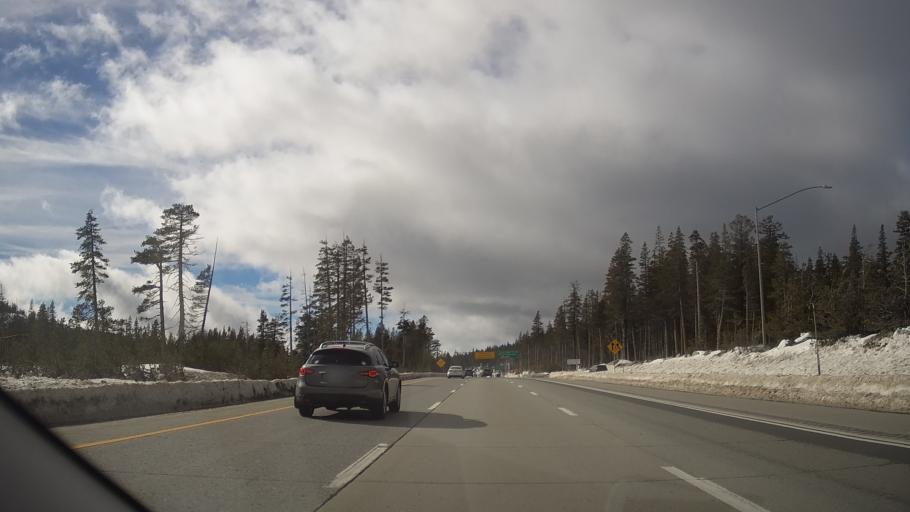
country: US
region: California
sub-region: Nevada County
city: Truckee
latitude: 39.3421
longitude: -120.3403
